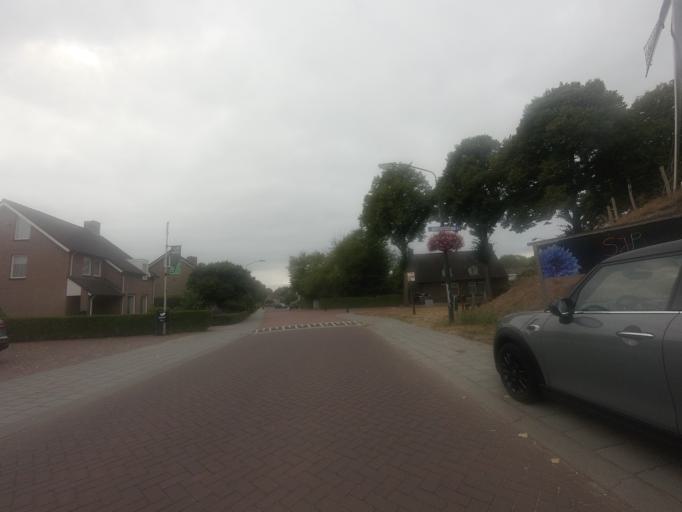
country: NL
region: North Brabant
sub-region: Gemeente Landerd
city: Zeeland
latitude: 51.6952
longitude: 5.6715
